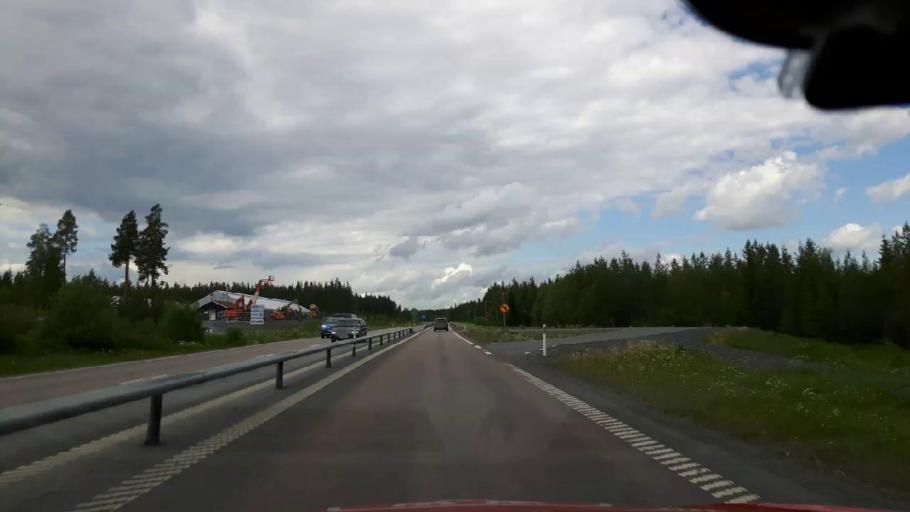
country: SE
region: Jaemtland
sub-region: OEstersunds Kommun
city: Ostersund
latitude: 63.2373
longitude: 14.6054
